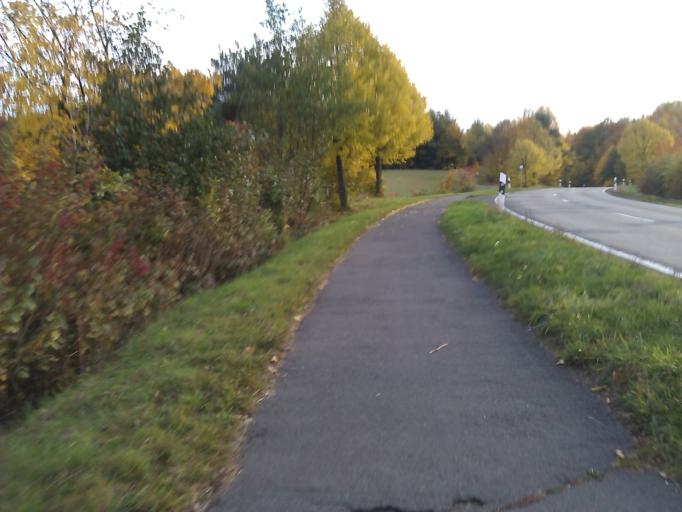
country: DE
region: Rheinland-Pfalz
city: Schneckenhausen
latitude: 49.5281
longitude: 7.7506
